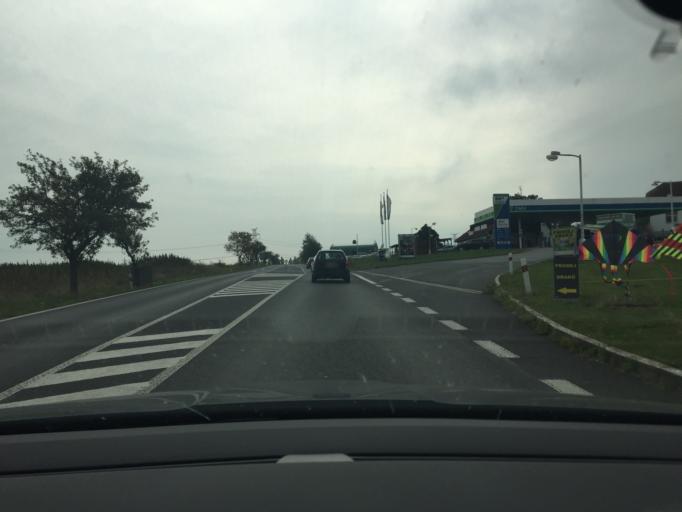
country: CZ
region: Central Bohemia
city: Milin
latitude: 49.5795
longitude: 14.0742
